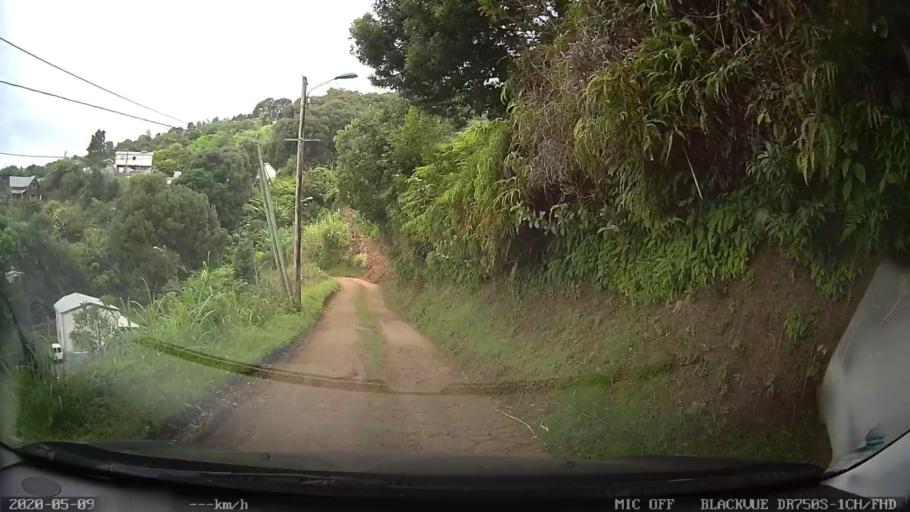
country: RE
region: Reunion
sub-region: Reunion
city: Sainte-Marie
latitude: -20.9498
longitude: 55.5289
